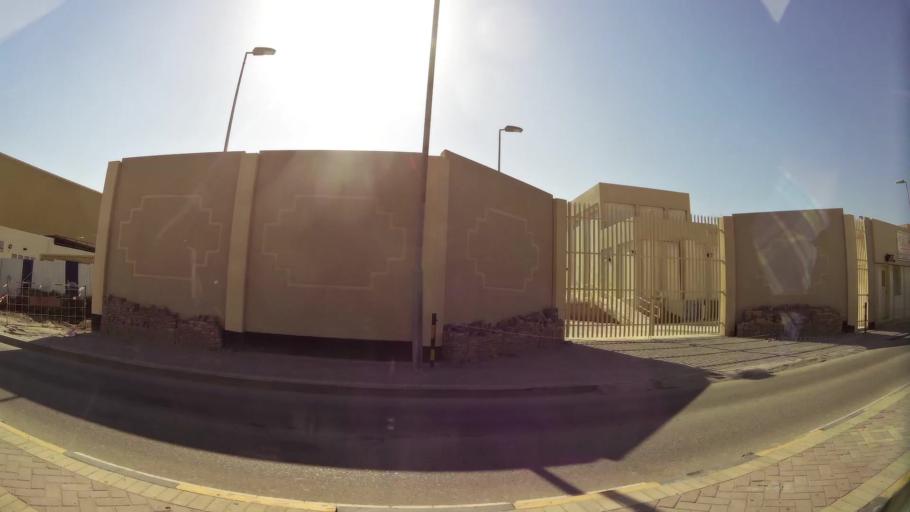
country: BH
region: Manama
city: Manama
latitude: 26.2161
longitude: 50.5748
